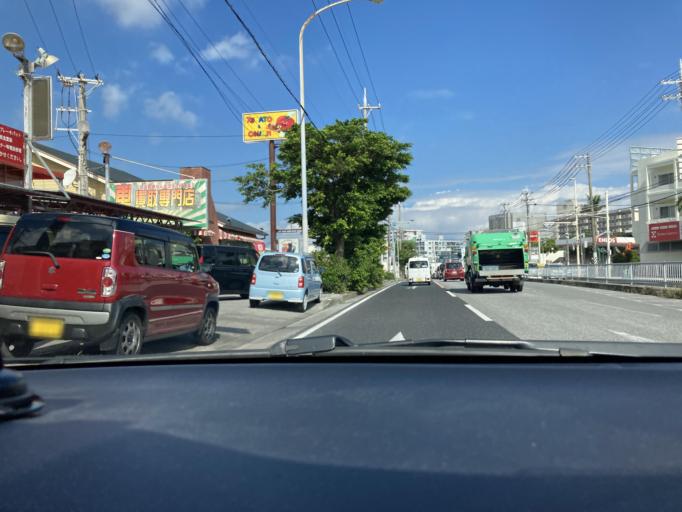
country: JP
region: Okinawa
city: Naha-shi
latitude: 26.2341
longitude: 127.7016
